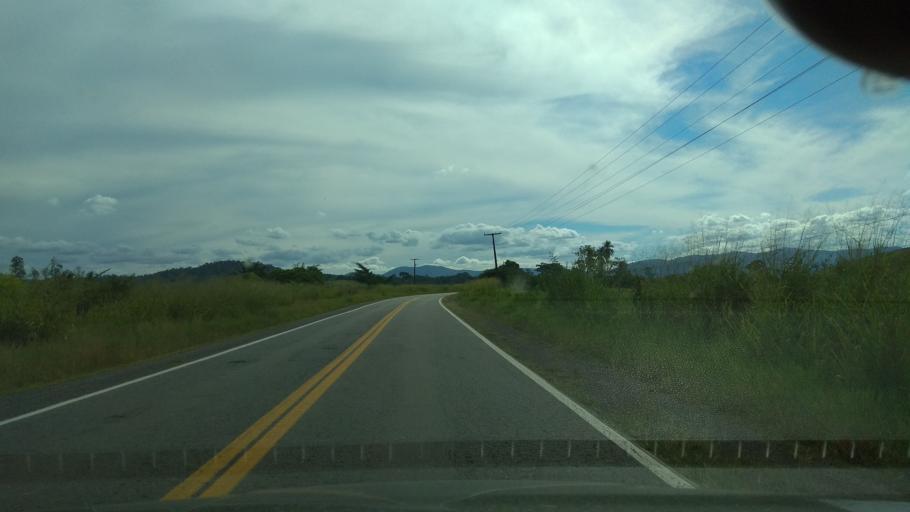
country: BR
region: Bahia
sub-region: Jitauna
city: Jitauna
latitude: -14.0411
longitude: -39.8221
